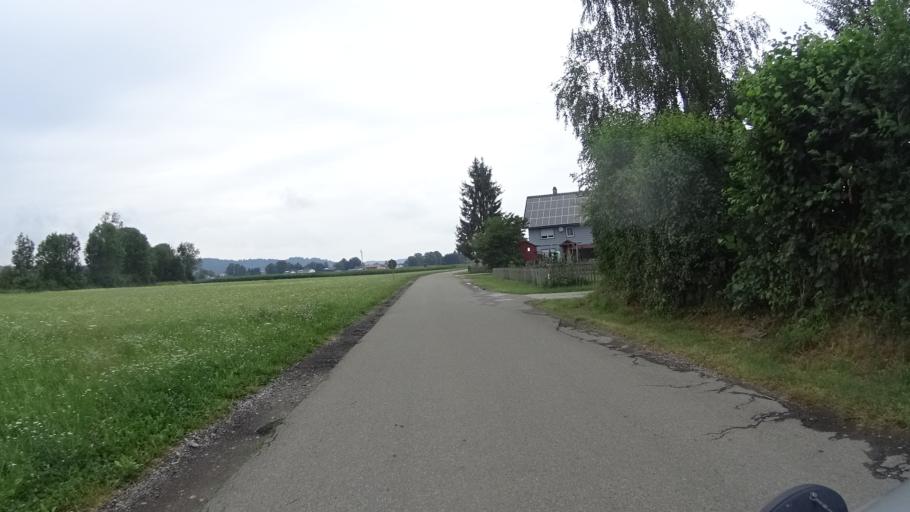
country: DE
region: Baden-Wuerttemberg
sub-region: Tuebingen Region
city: Kirchberg an der Iller
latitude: 48.1403
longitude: 10.1020
